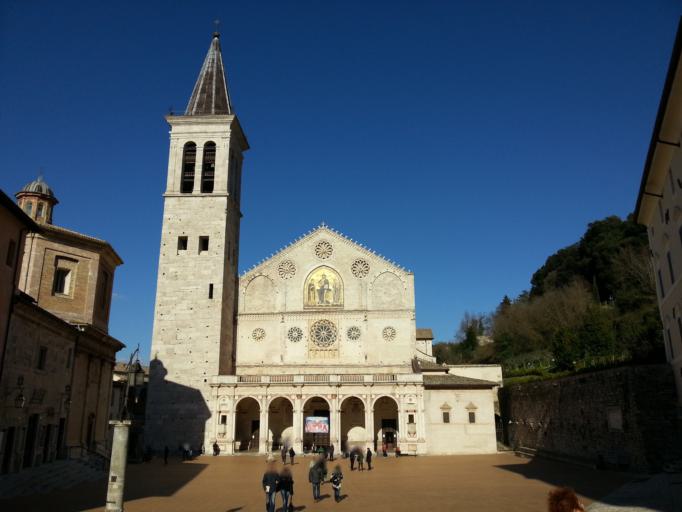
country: IT
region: Umbria
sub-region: Provincia di Perugia
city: Spoleto
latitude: 42.7344
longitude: 12.7389
